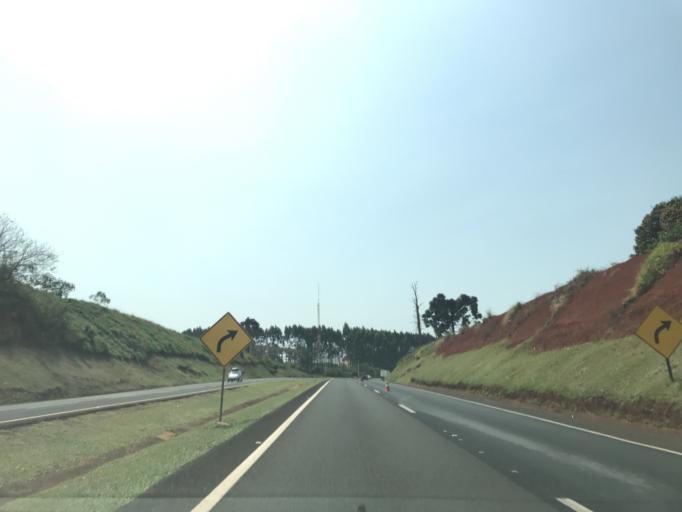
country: BR
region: Parana
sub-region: Rolandia
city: Rolandia
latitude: -23.3065
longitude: -51.3299
